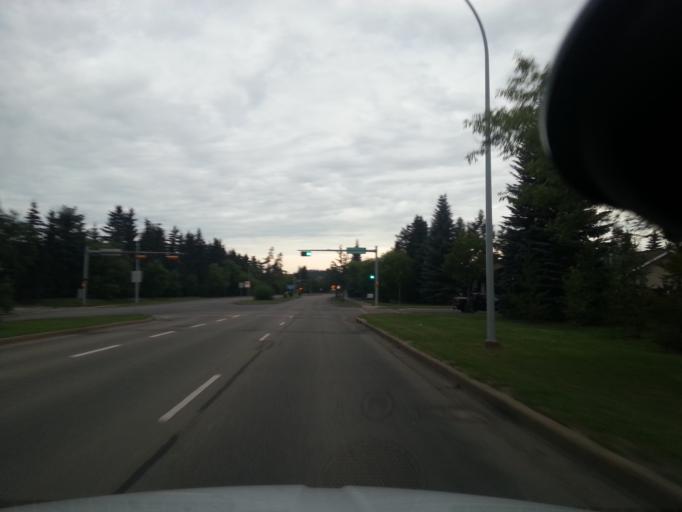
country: CA
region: Alberta
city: St. Albert
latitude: 53.6439
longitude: -113.6074
